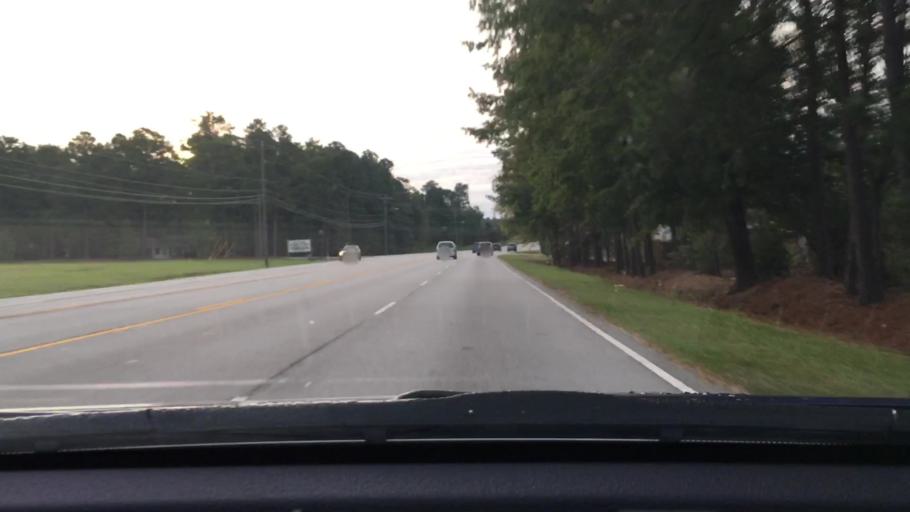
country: US
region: South Carolina
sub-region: Lexington County
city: Saint Andrews
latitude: 34.0794
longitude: -81.1303
